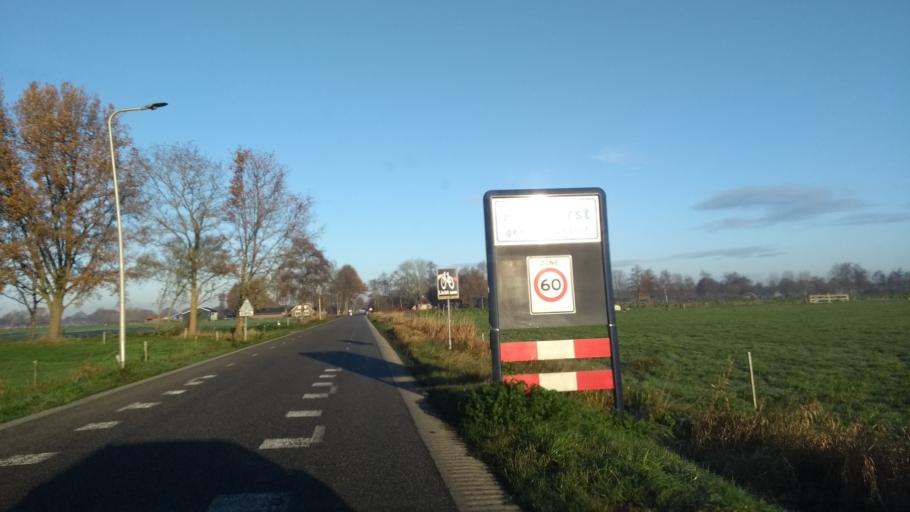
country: NL
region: Overijssel
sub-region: Gemeente Staphorst
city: Staphorst
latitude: 52.5962
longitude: 6.2842
